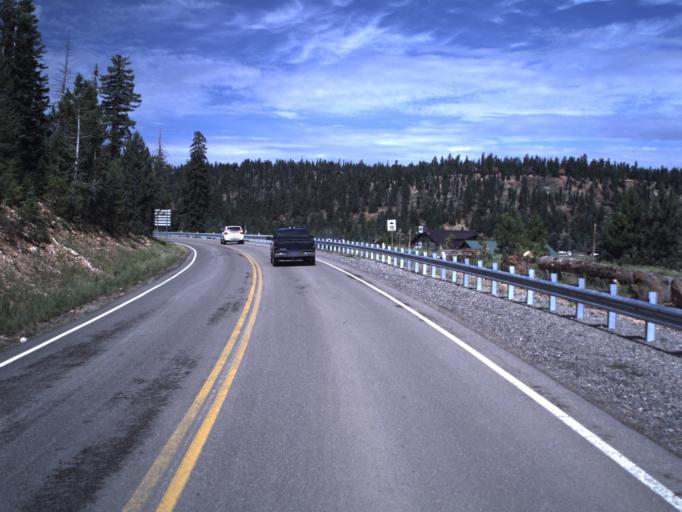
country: US
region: Utah
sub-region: Iron County
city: Parowan
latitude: 37.5247
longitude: -112.6618
